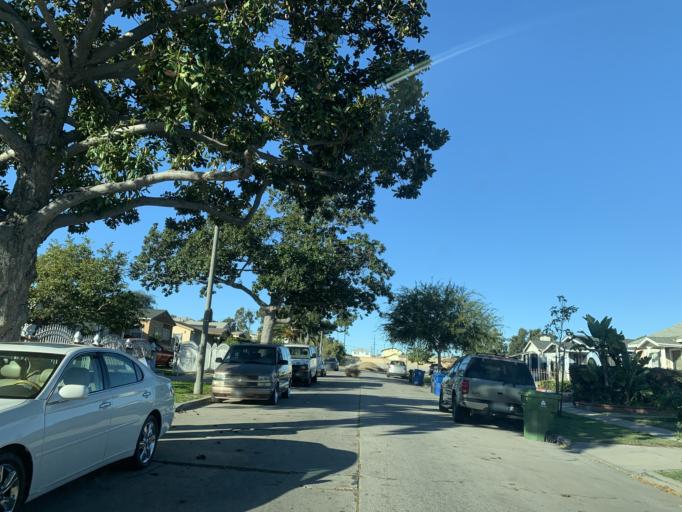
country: US
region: California
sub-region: Los Angeles County
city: West Athens
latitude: 33.9247
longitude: -118.2794
